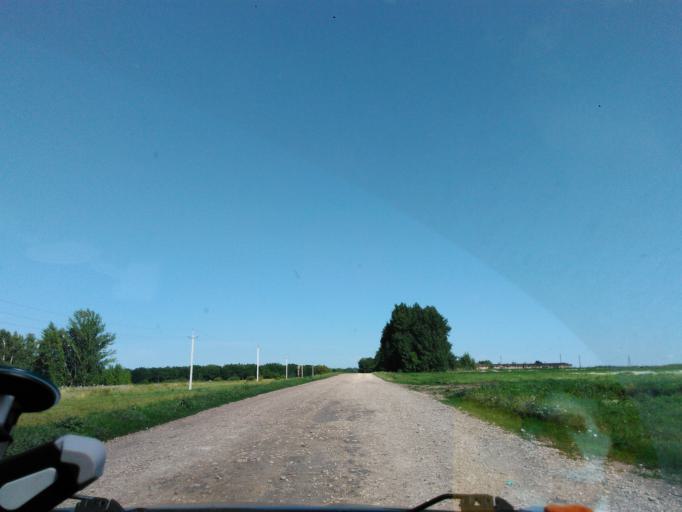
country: RU
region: Penza
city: Lermontovo
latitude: 52.9840
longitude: 43.6560
